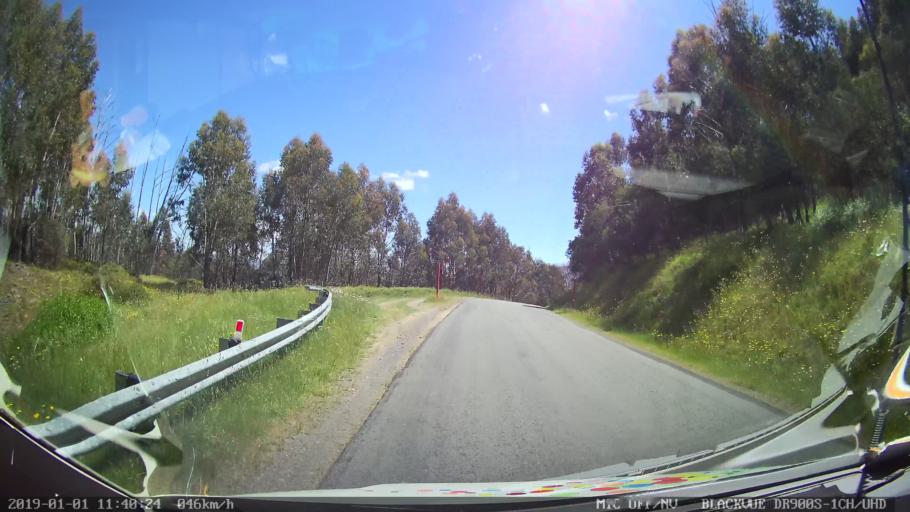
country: AU
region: New South Wales
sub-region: Snowy River
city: Jindabyne
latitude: -35.9205
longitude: 148.3868
